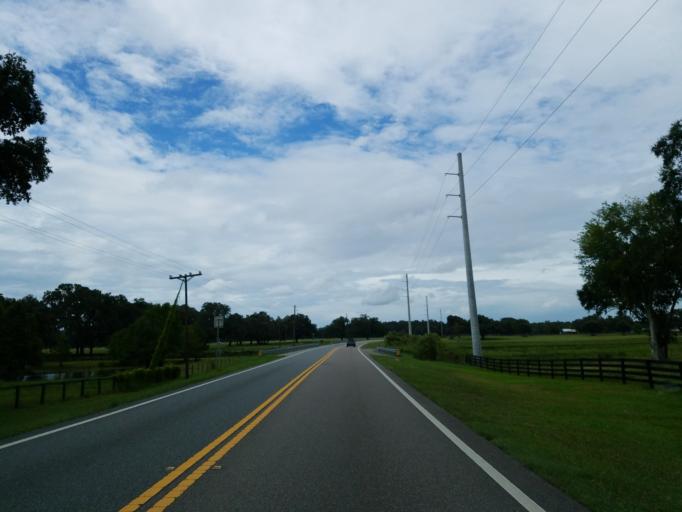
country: US
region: Florida
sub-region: Sumter County
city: Lake Panasoffkee
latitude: 28.8309
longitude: -82.1780
